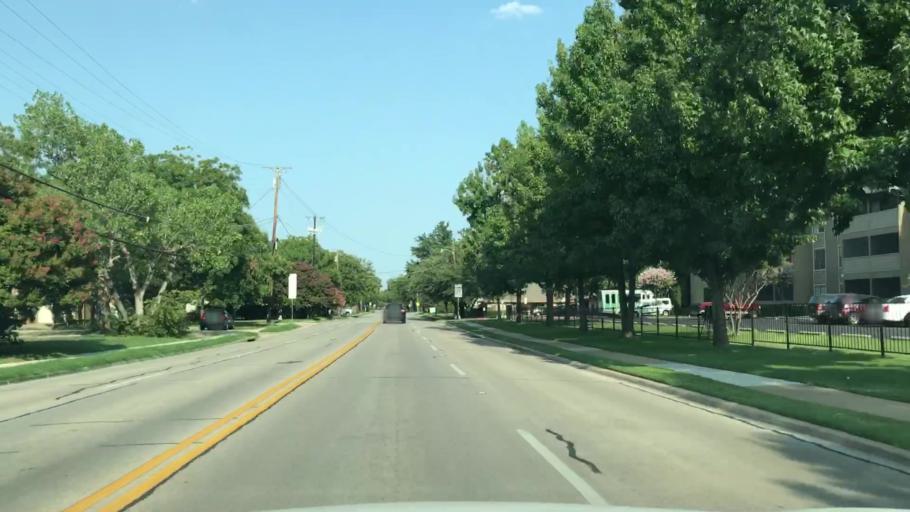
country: US
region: Texas
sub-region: Dallas County
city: Irving
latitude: 32.8221
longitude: -96.9421
